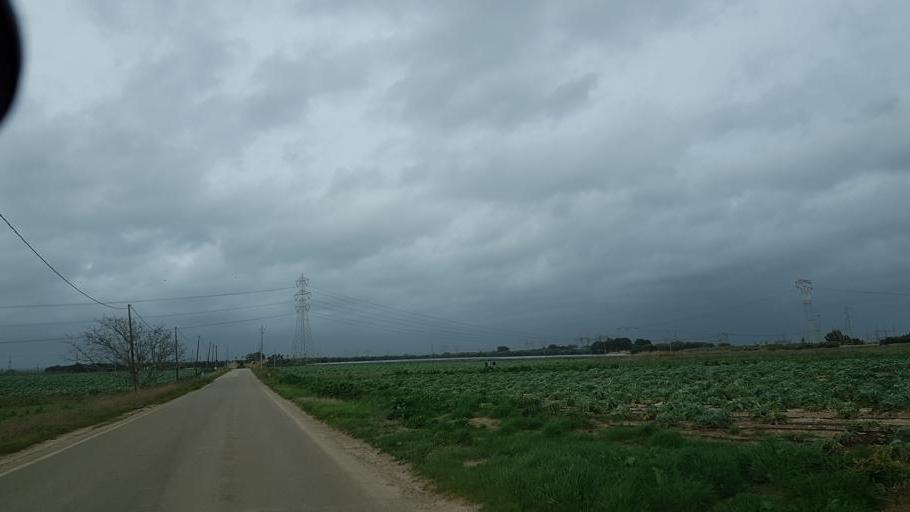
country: IT
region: Apulia
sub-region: Provincia di Brindisi
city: La Rosa
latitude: 40.5938
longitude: 17.9072
